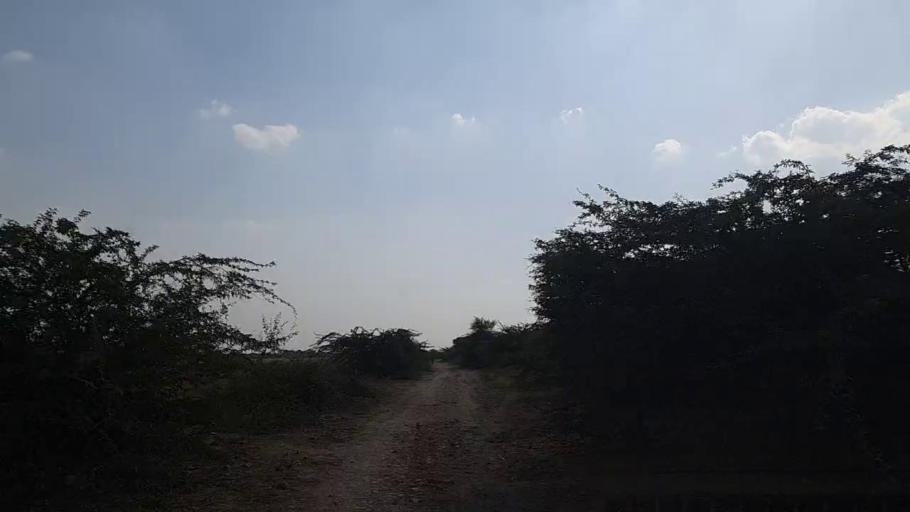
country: PK
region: Sindh
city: Jati
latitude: 24.4856
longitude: 68.3429
